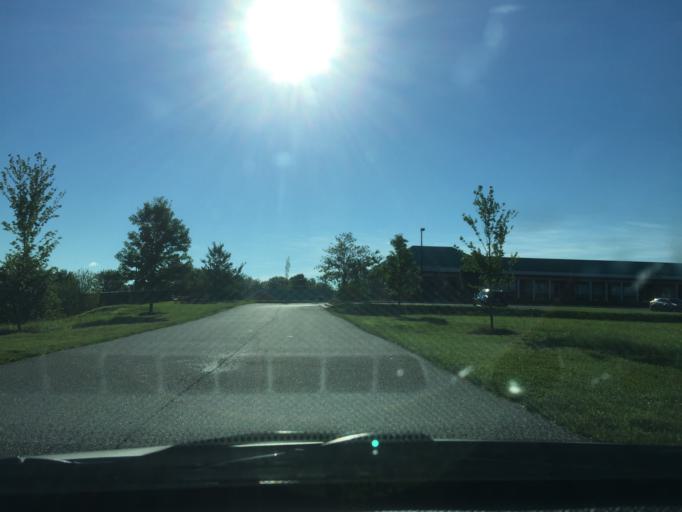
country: US
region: Maryland
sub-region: Baltimore County
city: Hunt Valley
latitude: 39.5119
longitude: -76.6436
